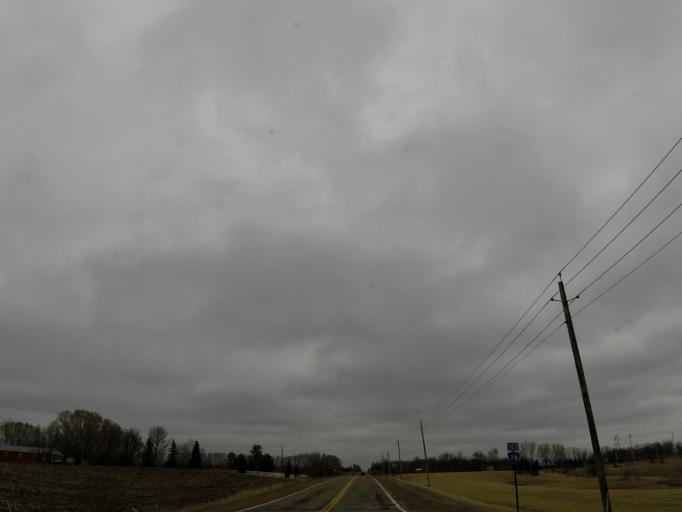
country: US
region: Minnesota
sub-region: Scott County
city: Shakopee
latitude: 44.7647
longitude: -93.5409
